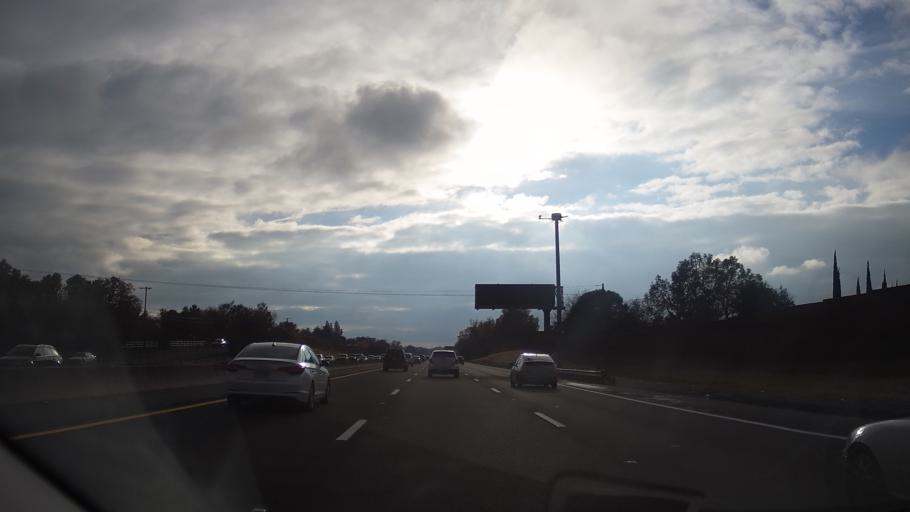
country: US
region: California
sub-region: Placer County
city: Rocklin
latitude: 38.7847
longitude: -121.2274
